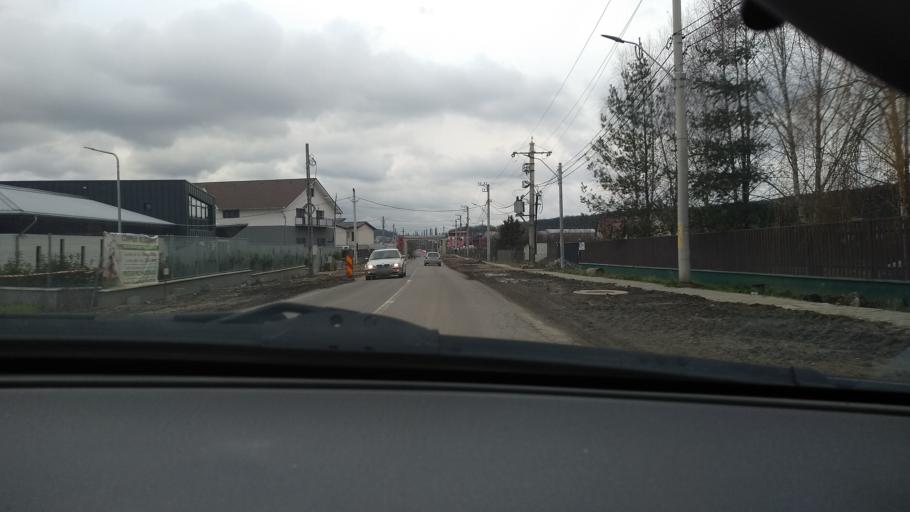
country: RO
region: Mures
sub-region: Comuna Livezeni
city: Livezeni
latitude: 46.5441
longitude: 24.6173
